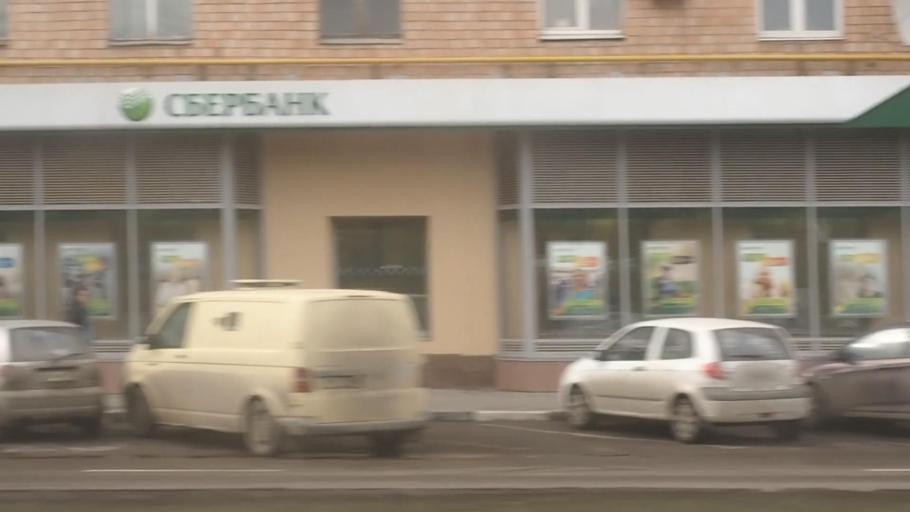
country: RU
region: Moskovskaya
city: Leninskiye Gory
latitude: 55.6986
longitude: 37.5634
